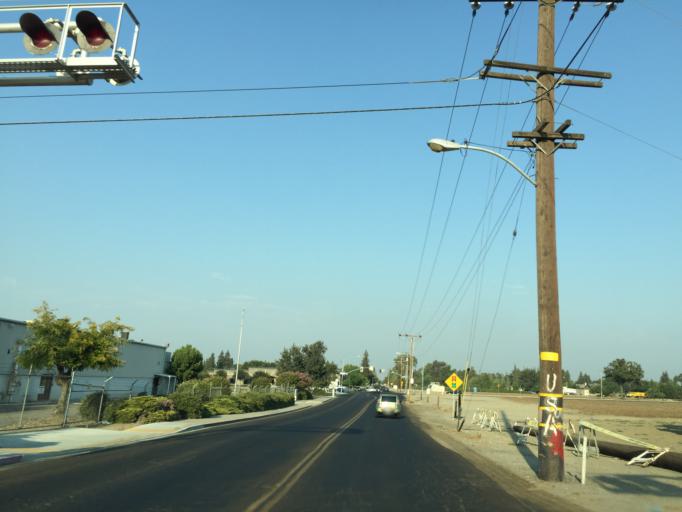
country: US
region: California
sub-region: Tulare County
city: Visalia
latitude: 36.3201
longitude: -119.2788
